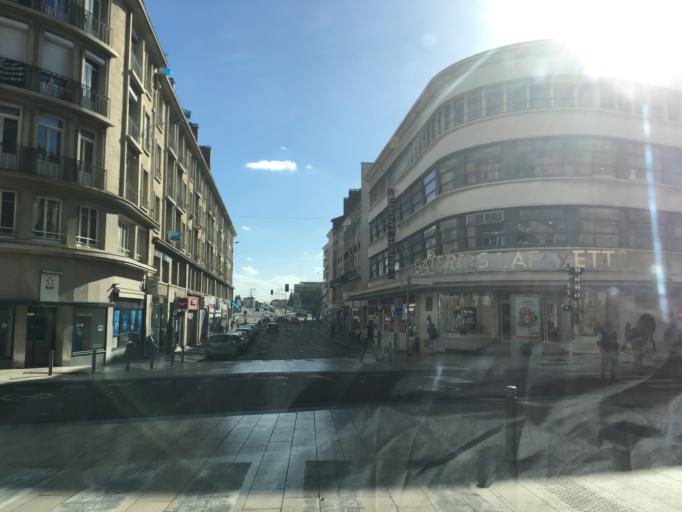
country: FR
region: Haute-Normandie
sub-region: Departement de la Seine-Maritime
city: Rouen
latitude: 49.4397
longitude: 1.0929
